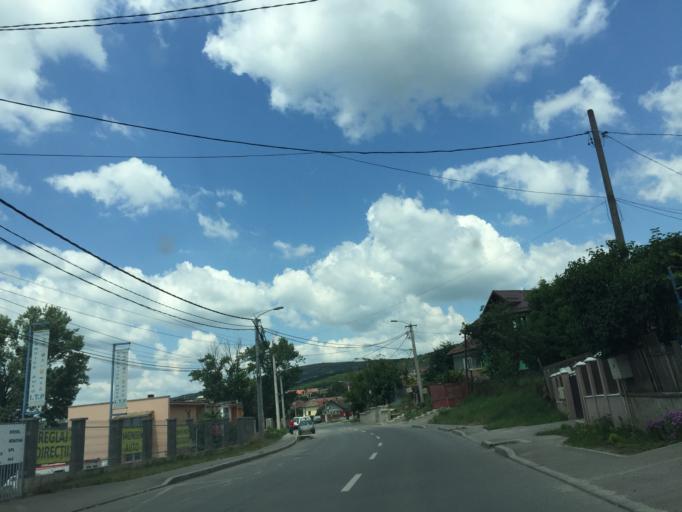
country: RO
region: Cluj
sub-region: Municipiul Cluj-Napoca
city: Cluj-Napoca
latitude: 46.8081
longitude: 23.6061
